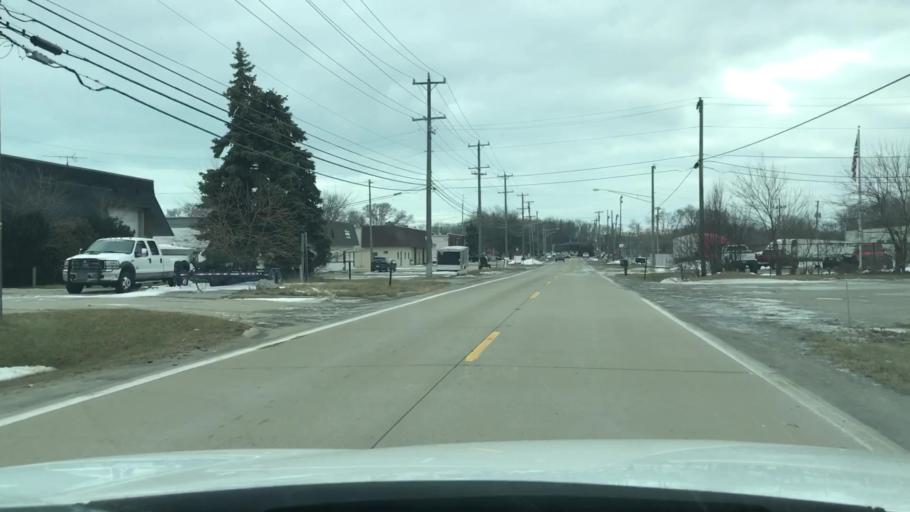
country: US
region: Michigan
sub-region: Macomb County
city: Mount Clemens
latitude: 42.5958
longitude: -82.8537
